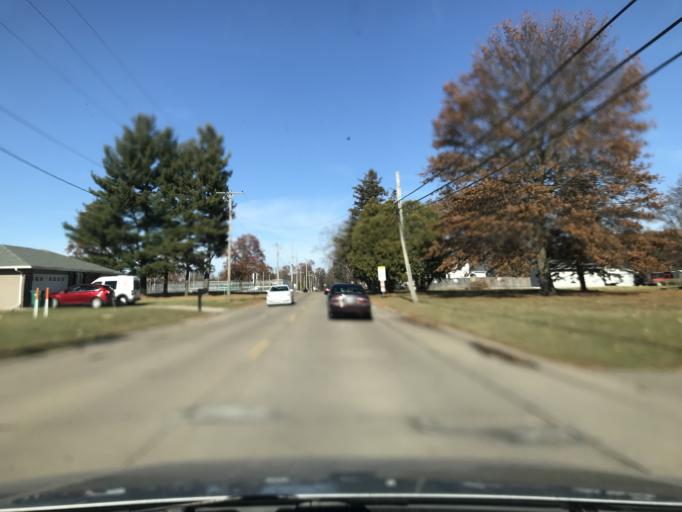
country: US
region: Illinois
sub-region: McDonough County
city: Macomb
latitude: 40.4424
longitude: -90.6709
